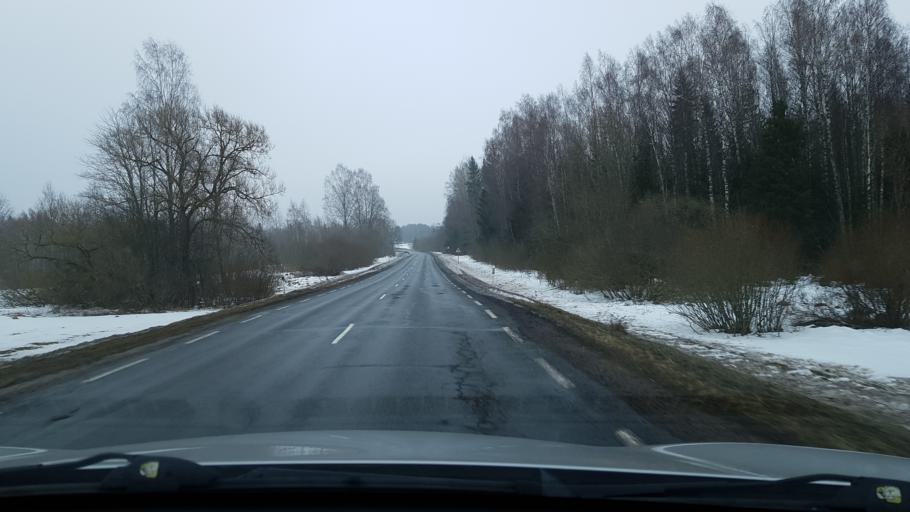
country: EE
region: Viljandimaa
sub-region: Viiratsi vald
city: Viiratsi
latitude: 58.2523
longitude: 25.7360
